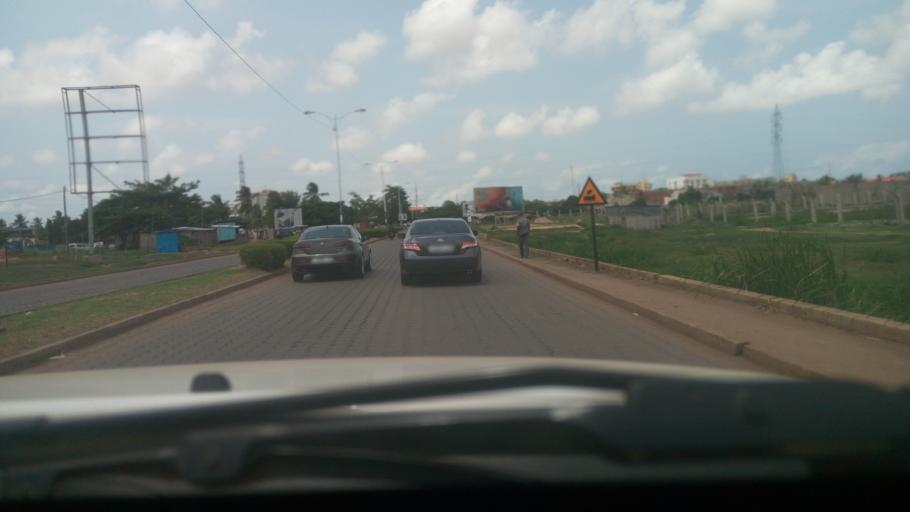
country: TG
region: Maritime
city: Lome
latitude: 6.1956
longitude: 1.2047
